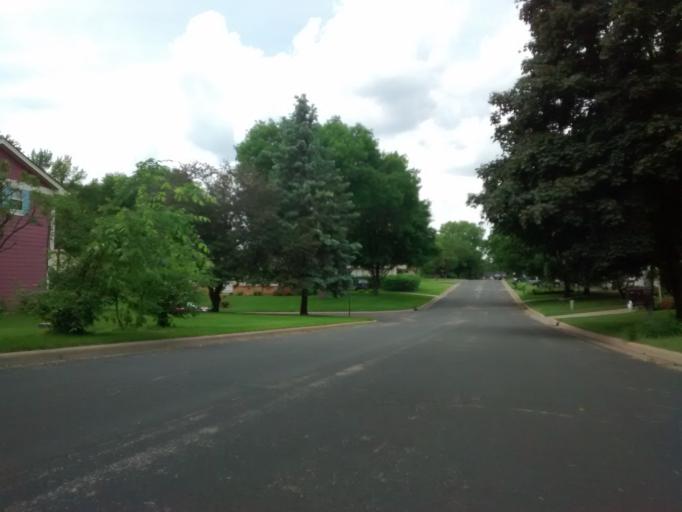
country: US
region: Minnesota
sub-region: Dakota County
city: Burnsville
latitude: 44.7579
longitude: -93.2927
